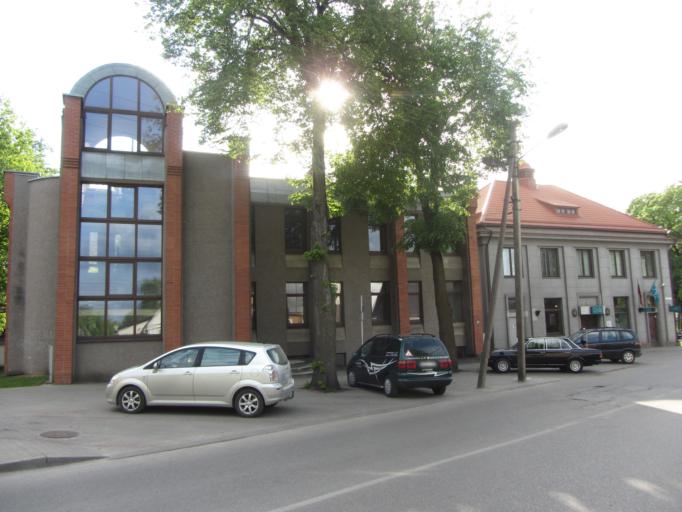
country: LT
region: Utenos apskritis
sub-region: Utena
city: Utena
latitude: 55.4984
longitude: 25.6035
